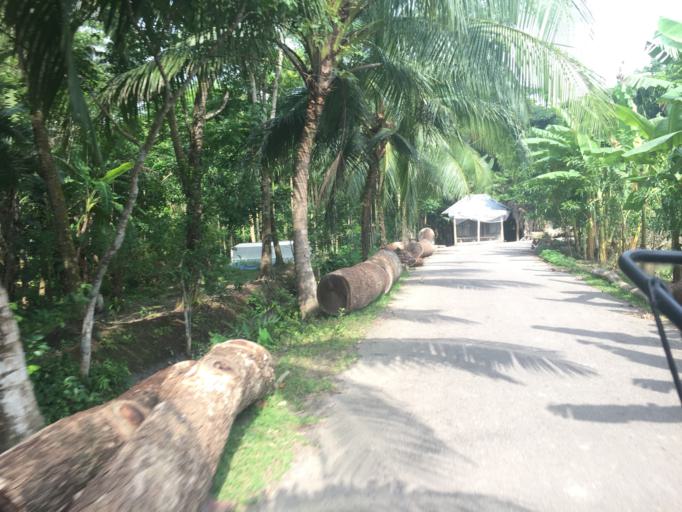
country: BD
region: Barisal
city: Mathba
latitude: 22.2531
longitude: 89.9128
